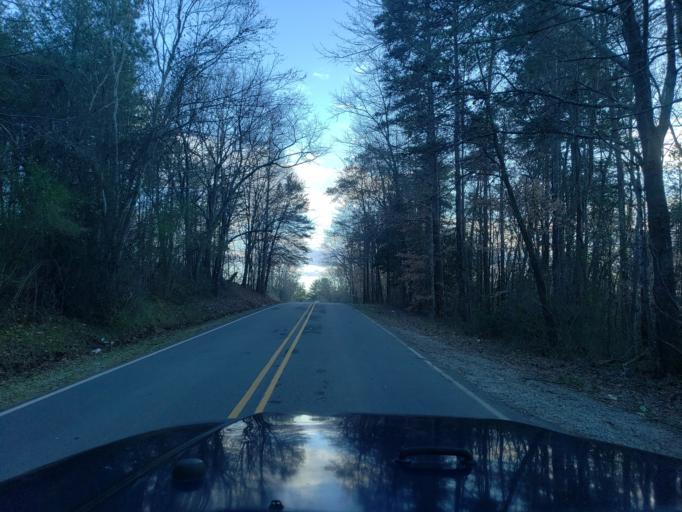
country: US
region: North Carolina
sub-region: Cleveland County
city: Shelby
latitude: 35.4186
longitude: -81.5684
